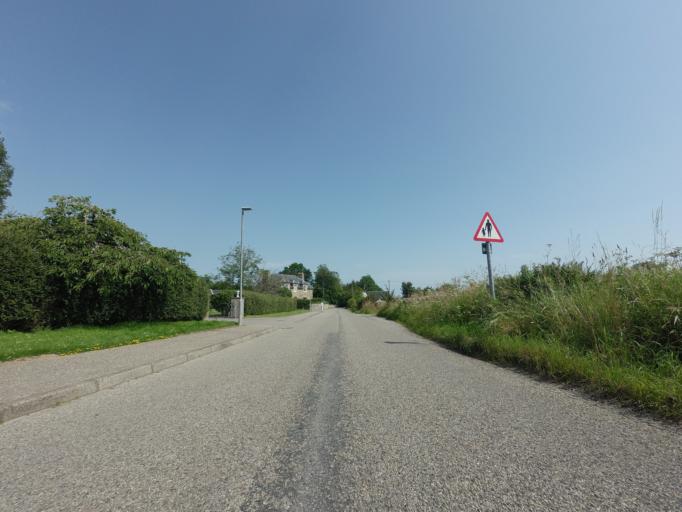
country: GB
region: Scotland
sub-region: Highland
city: Tain
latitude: 57.8031
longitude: -4.0653
